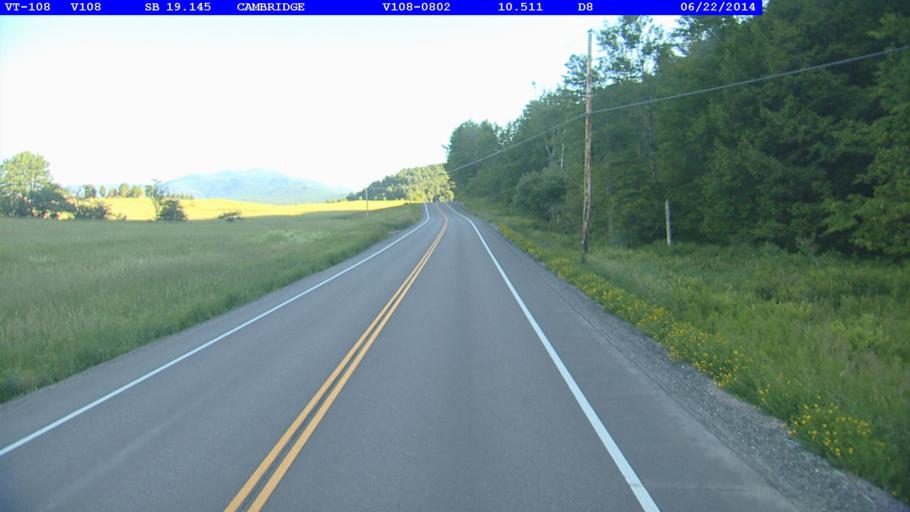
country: US
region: Vermont
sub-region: Lamoille County
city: Johnson
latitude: 44.6670
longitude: -72.8286
